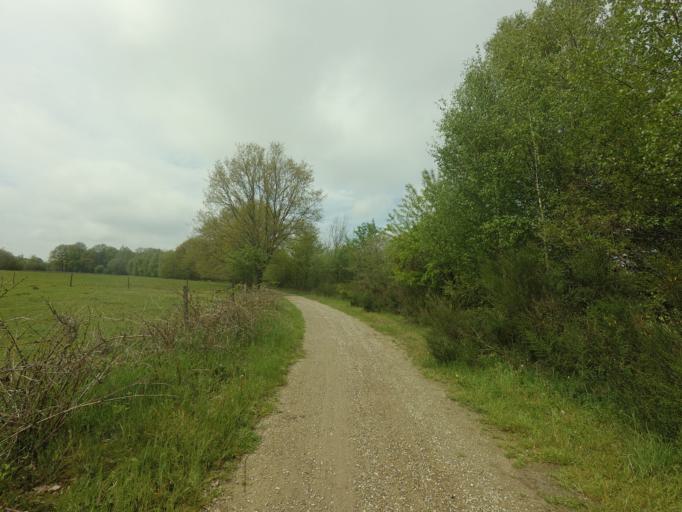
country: NL
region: Overijssel
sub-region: Gemeente Haaksbergen
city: Haaksbergen
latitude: 52.1371
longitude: 6.7867
